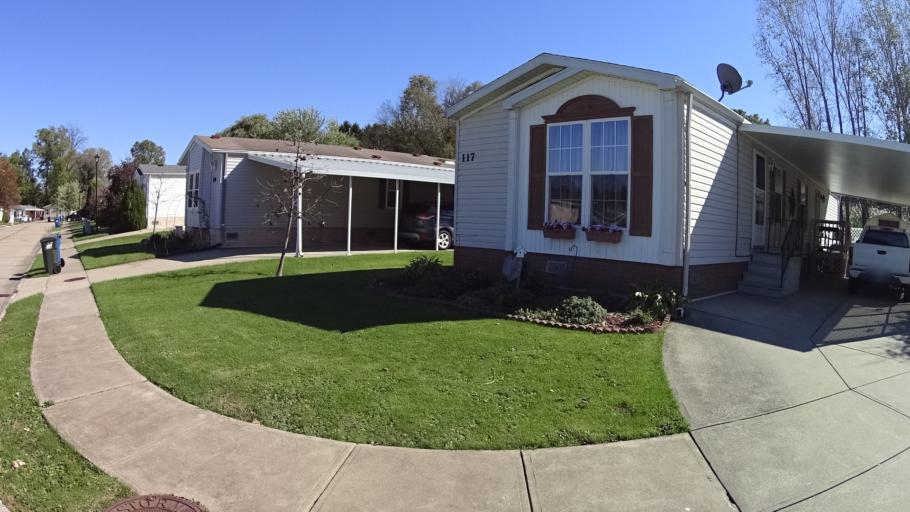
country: US
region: Ohio
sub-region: Lorain County
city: Amherst
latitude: 41.4097
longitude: -82.2012
